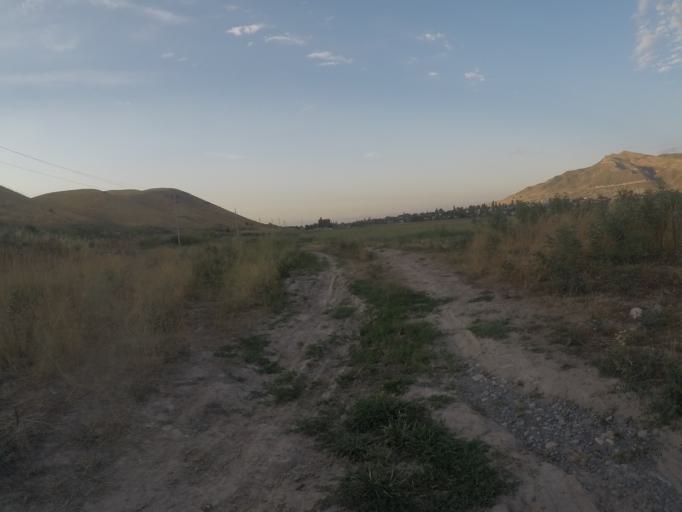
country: KG
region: Chuy
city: Bishkek
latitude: 42.7595
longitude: 74.6360
